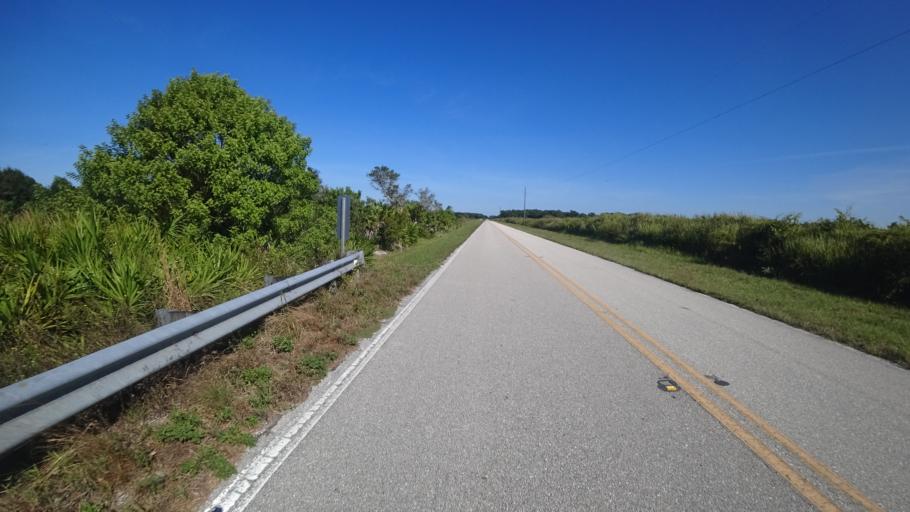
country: US
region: Florida
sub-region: Hillsborough County
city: Wimauma
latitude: 27.6116
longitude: -82.2927
